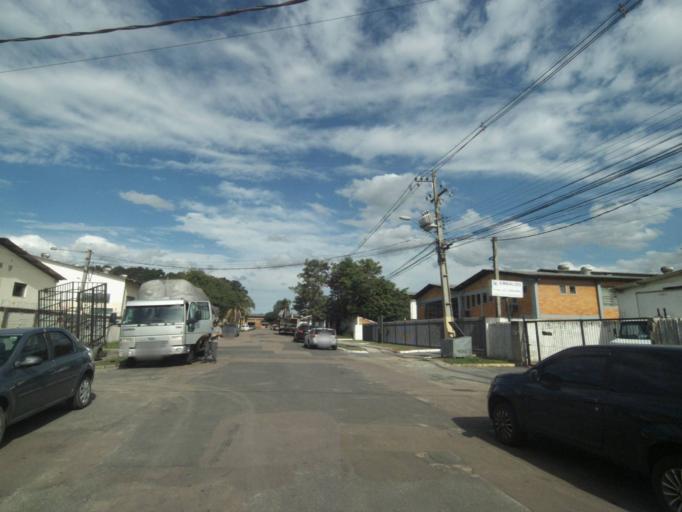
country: BR
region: Parana
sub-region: Curitiba
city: Curitiba
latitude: -25.4993
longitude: -49.3314
